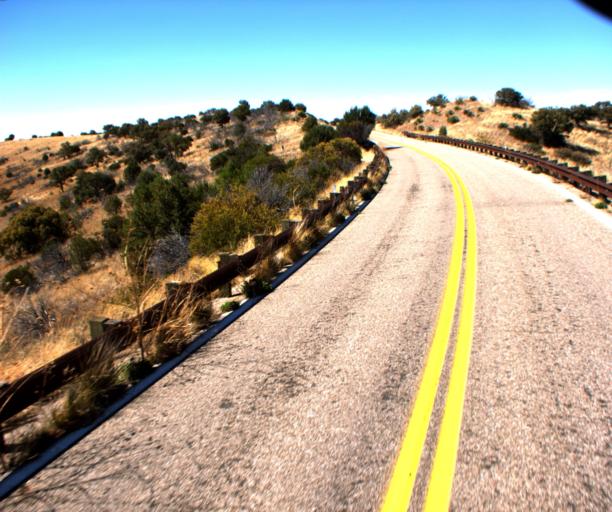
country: US
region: Arizona
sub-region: Cochise County
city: Sierra Vista
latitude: 31.5091
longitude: -110.4958
